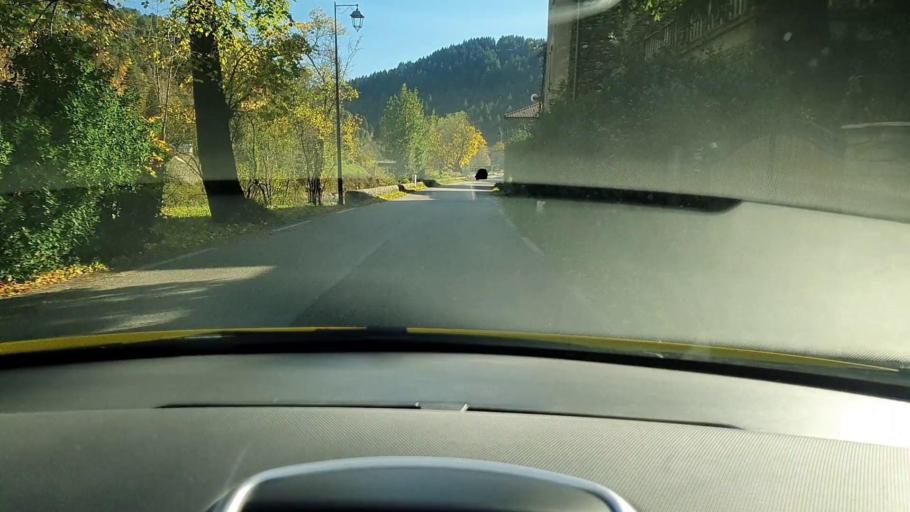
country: FR
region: Languedoc-Roussillon
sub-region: Departement du Gard
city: Lasalle
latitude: 44.1172
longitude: 3.7642
